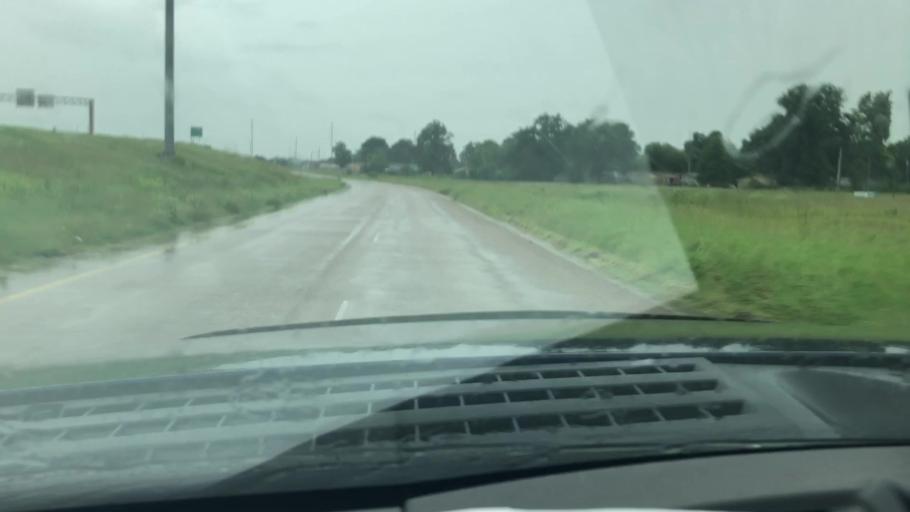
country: US
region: Texas
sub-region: Bowie County
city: Wake Village
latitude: 33.3885
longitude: -94.0961
